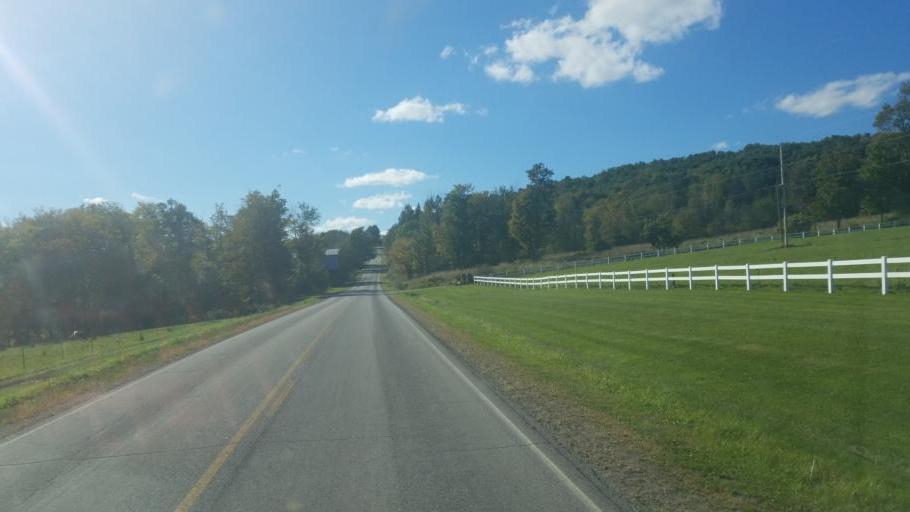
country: US
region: New York
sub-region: Allegany County
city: Friendship
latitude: 42.2756
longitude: -78.1460
